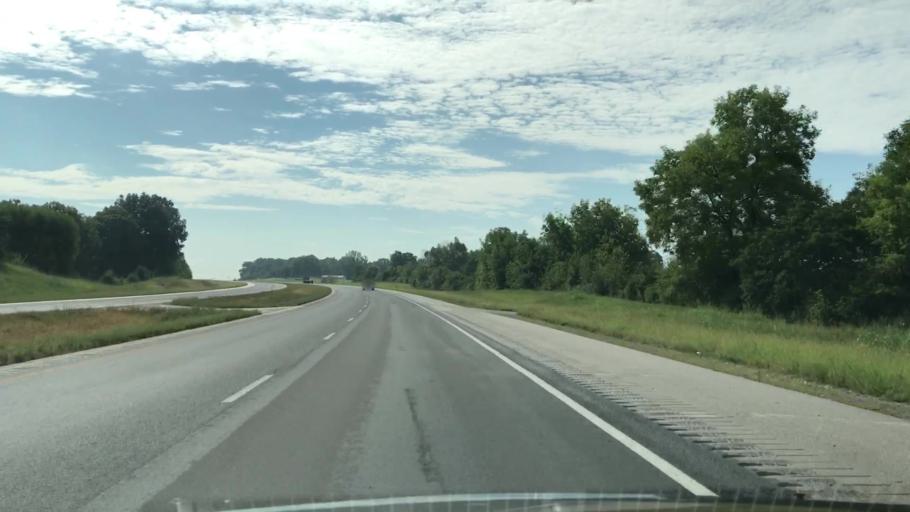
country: US
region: Kentucky
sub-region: Warren County
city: Plano
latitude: 36.8649
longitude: -86.3506
